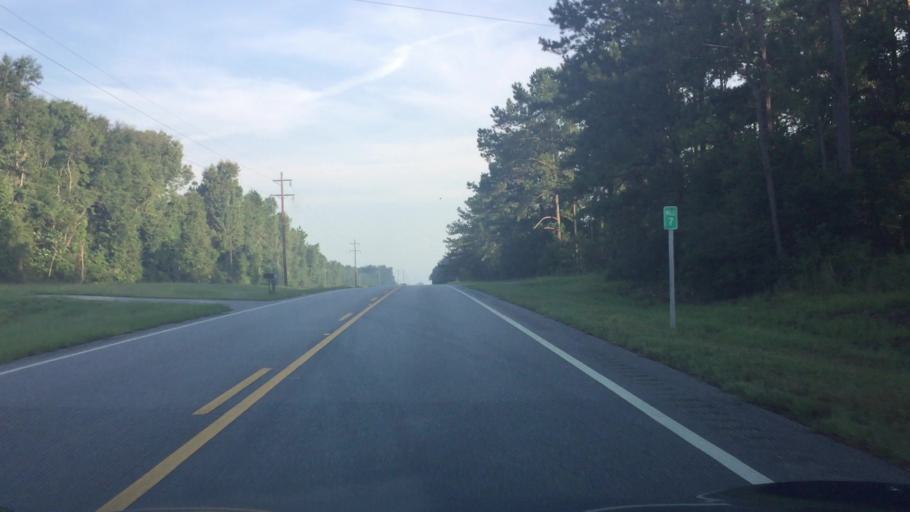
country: US
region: Alabama
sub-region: Covington County
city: Florala
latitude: 31.0631
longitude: -86.3969
